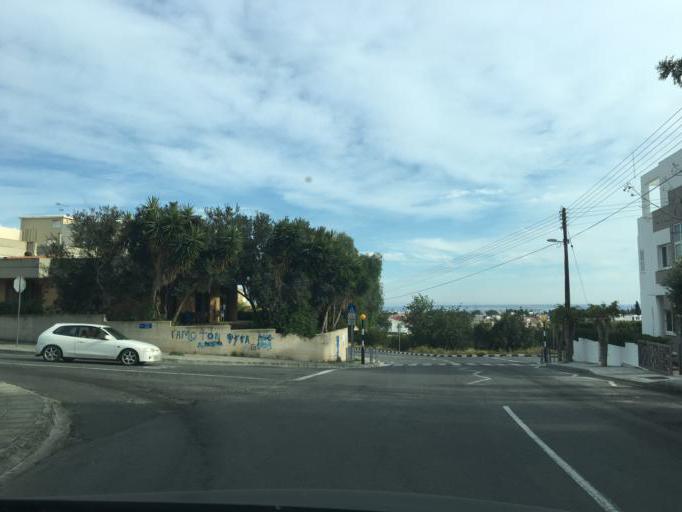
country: CY
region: Limassol
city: Pano Polemidia
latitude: 34.7076
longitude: 33.0062
